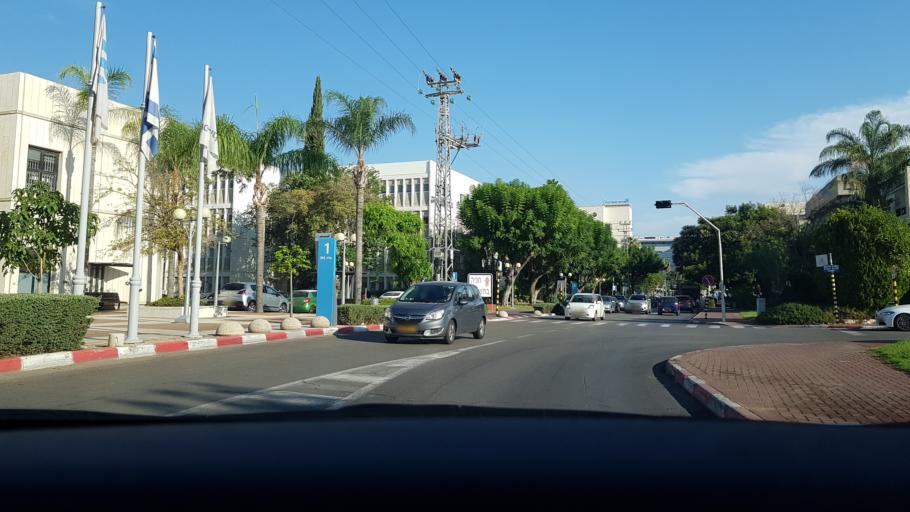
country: IL
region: Central District
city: Ness Ziona
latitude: 31.9138
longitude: 34.8036
